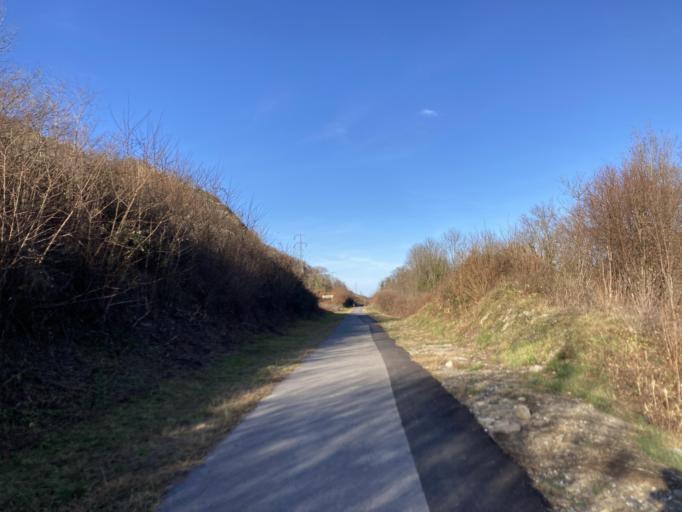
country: FR
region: Aquitaine
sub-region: Departement des Pyrenees-Atlantiques
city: Louvie-Juzon
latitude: 43.0654
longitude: -0.4247
